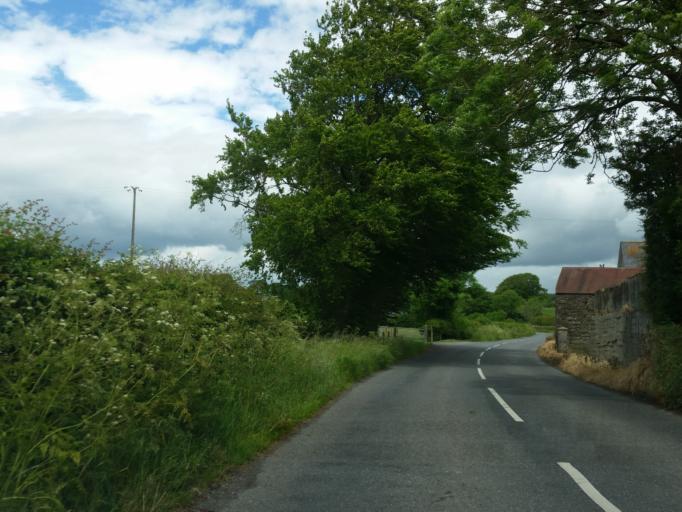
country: GB
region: Northern Ireland
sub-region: Omagh District
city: Omagh
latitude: 54.5503
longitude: -7.1183
